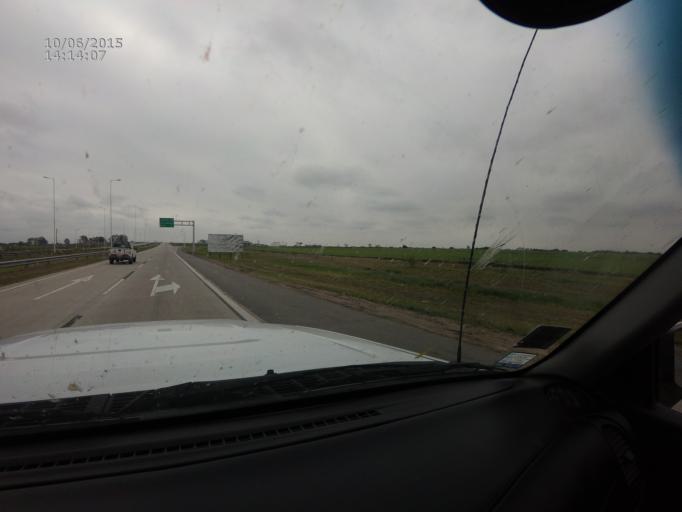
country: AR
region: Cordoba
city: Villa Maria
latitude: -32.4226
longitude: -63.1517
